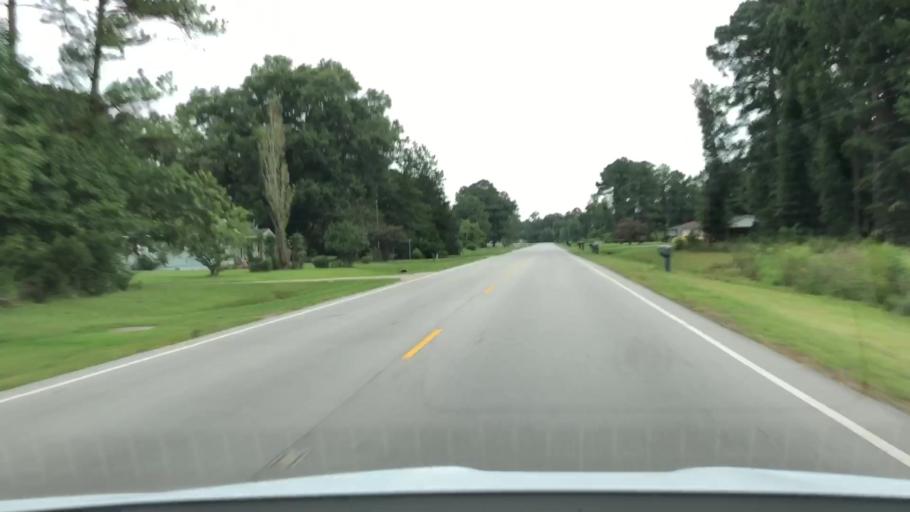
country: US
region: North Carolina
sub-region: Jones County
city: Trenton
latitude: 35.0227
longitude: -77.3054
